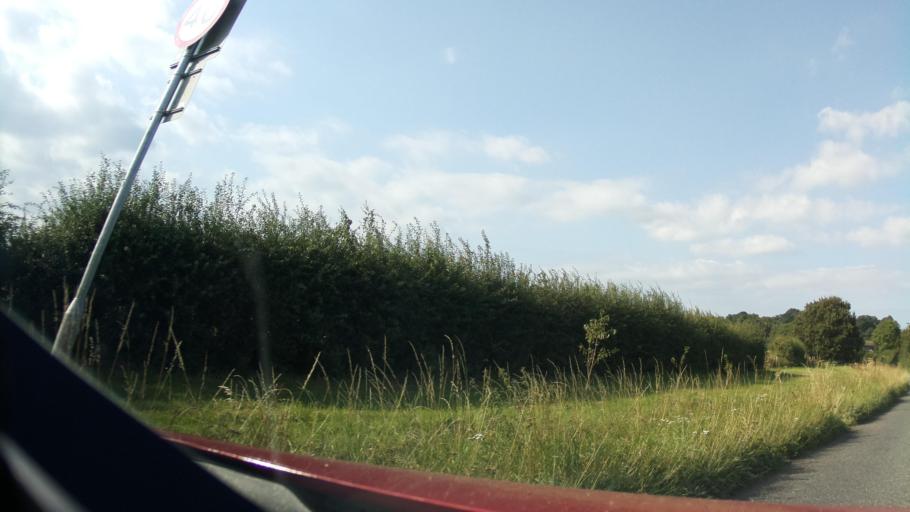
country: GB
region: England
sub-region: Devon
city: Heavitree
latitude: 50.7897
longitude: -3.4937
